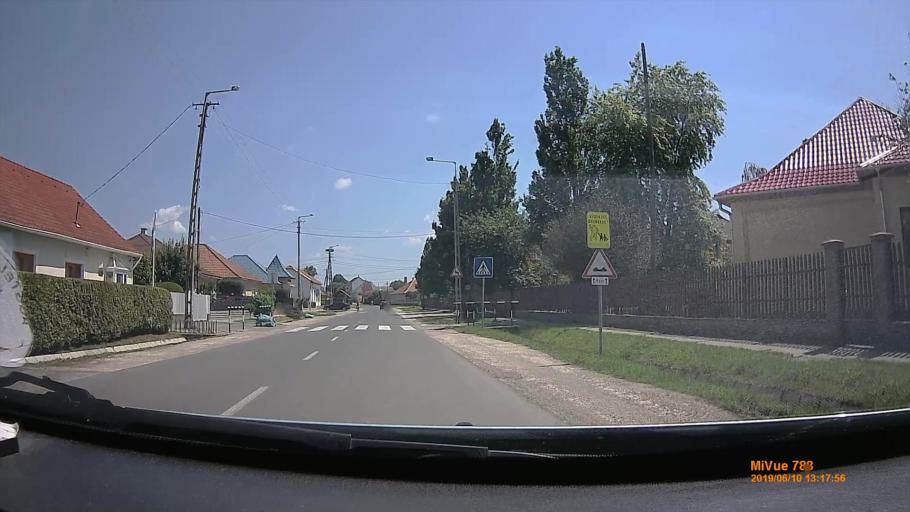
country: HU
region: Borsod-Abauj-Zemplen
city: Tiszaluc
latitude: 48.0364
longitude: 21.0638
